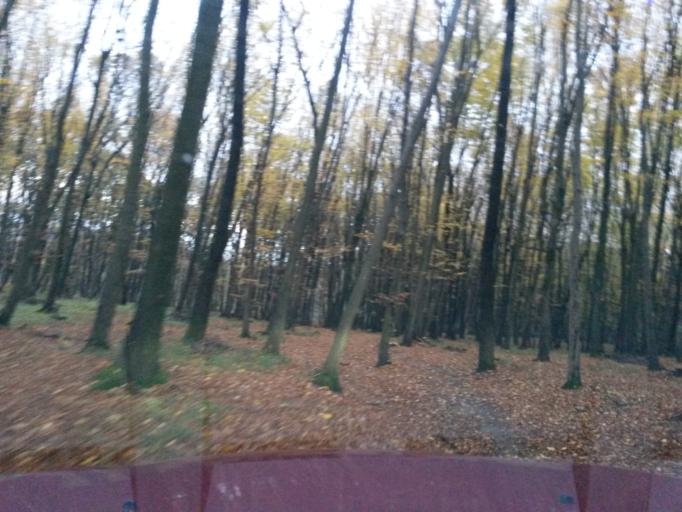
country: SK
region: Kosicky
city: Kosice
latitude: 48.7957
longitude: 21.2843
